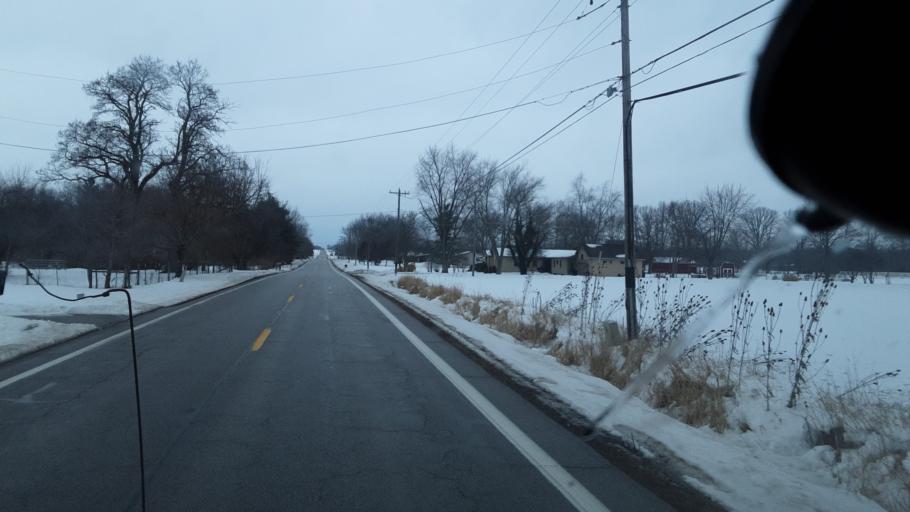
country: US
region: Ohio
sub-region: Madison County
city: Plain City
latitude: 40.1514
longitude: -83.3039
